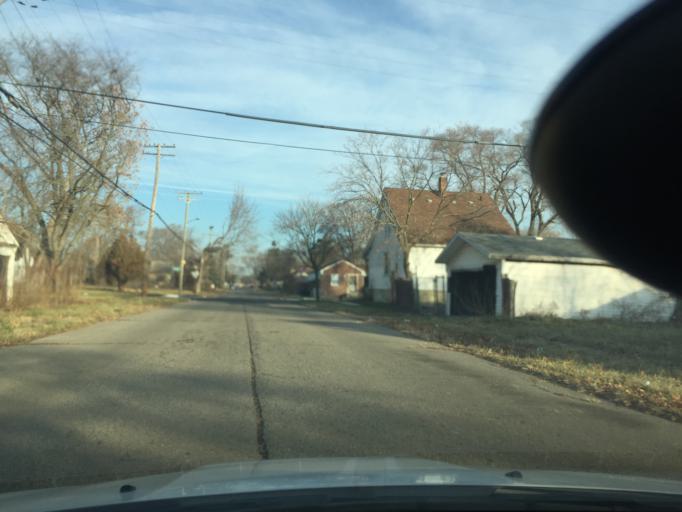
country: US
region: Michigan
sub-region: Macomb County
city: Eastpointe
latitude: 42.4395
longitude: -82.9688
